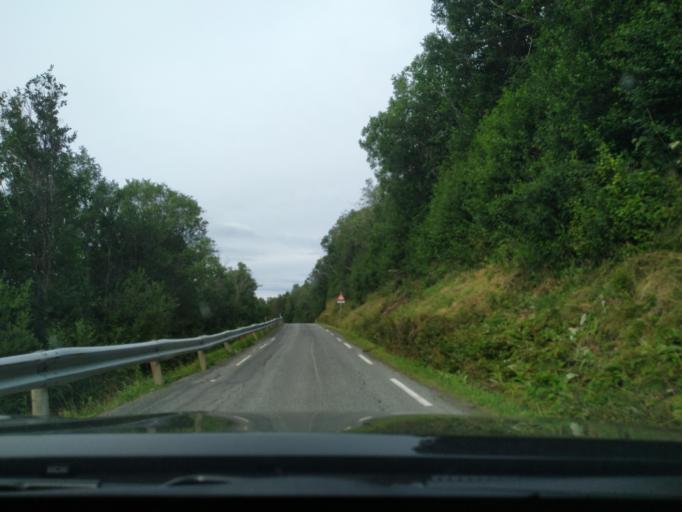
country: NO
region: Nordland
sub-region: Evenes
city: Randa
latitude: 68.7274
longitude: 16.8674
